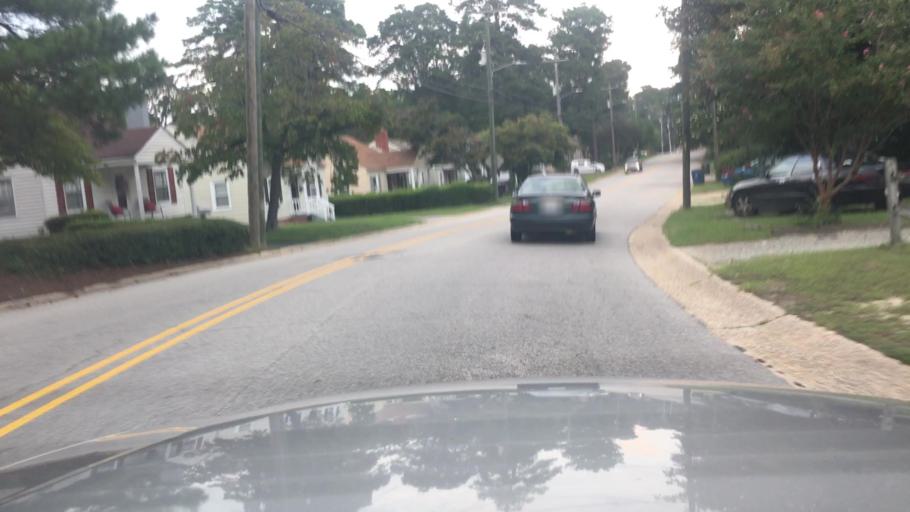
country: US
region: North Carolina
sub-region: Cumberland County
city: Fayetteville
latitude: 35.0579
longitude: -78.9178
